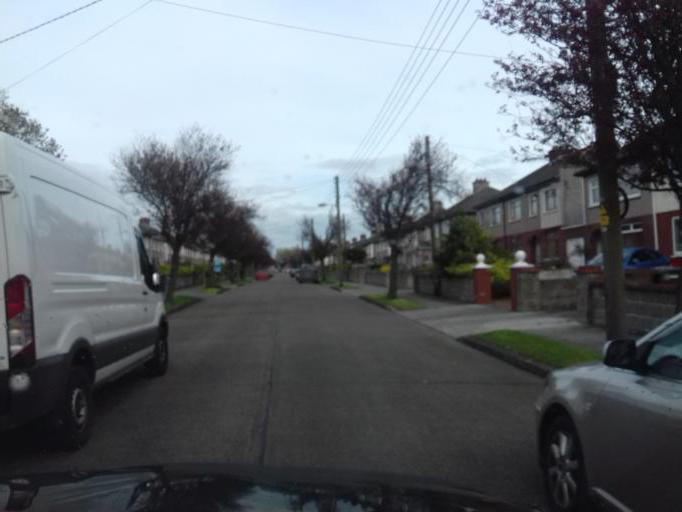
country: IE
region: Leinster
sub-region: Dublin City
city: Finglas
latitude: 53.3957
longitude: -6.2838
